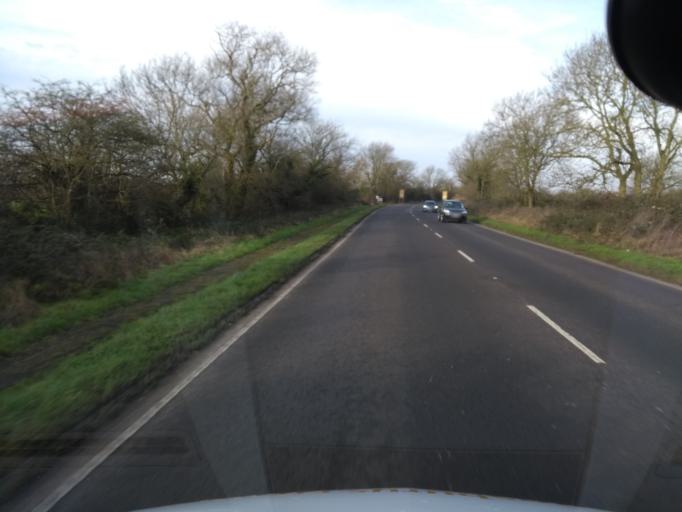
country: GB
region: England
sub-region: North Somerset
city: Bleadon
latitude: 51.2828
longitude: -2.9393
